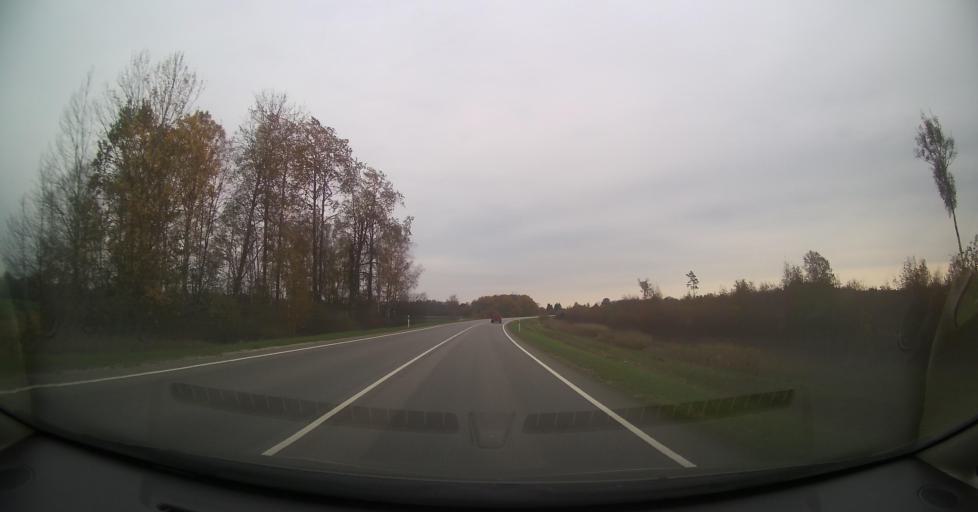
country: EE
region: Laeaene
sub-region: Ridala Parish
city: Uuemoisa
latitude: 58.9733
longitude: 23.8483
